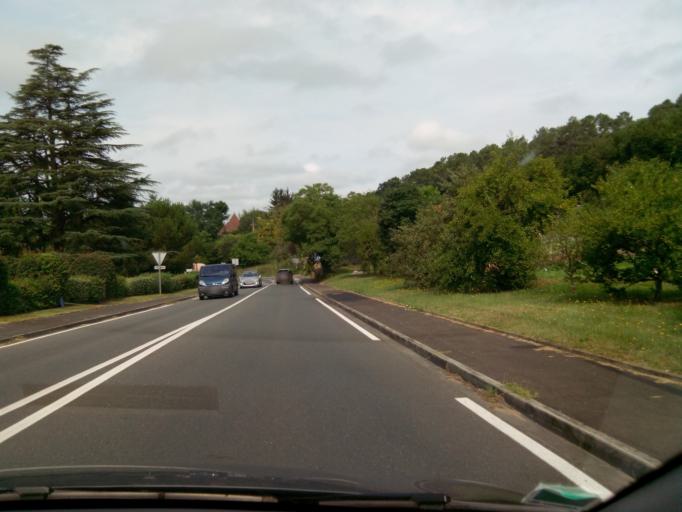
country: FR
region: Aquitaine
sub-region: Departement de la Dordogne
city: Carsac-Aillac
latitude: 44.8647
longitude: 1.2543
